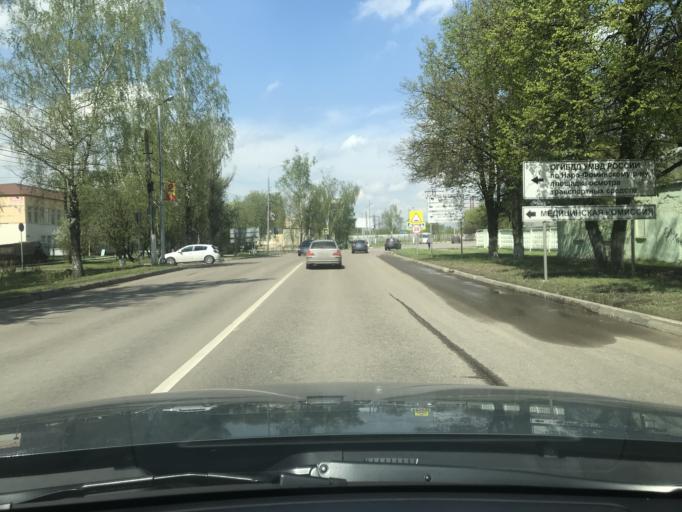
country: RU
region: Moskovskaya
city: Naro-Fominsk
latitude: 55.3809
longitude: 36.7565
